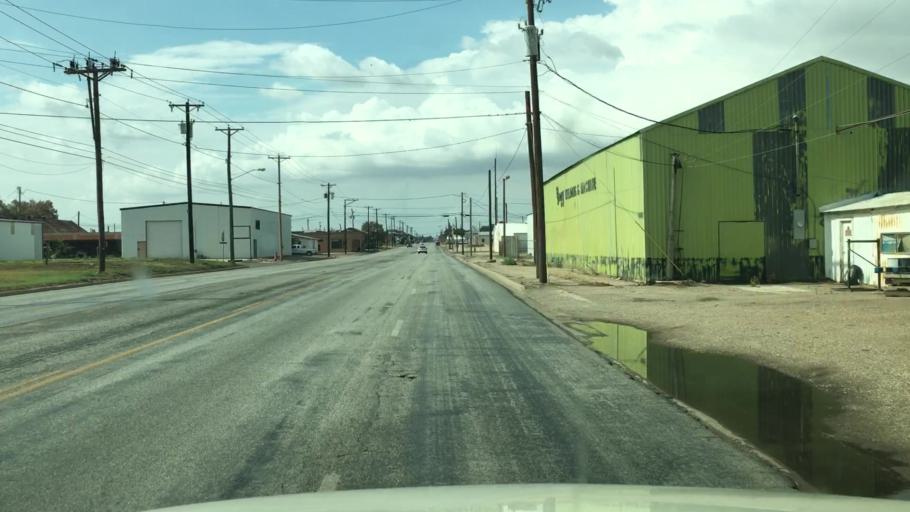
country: US
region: Texas
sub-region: Dawson County
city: Lamesa
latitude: 32.7321
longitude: -101.9487
